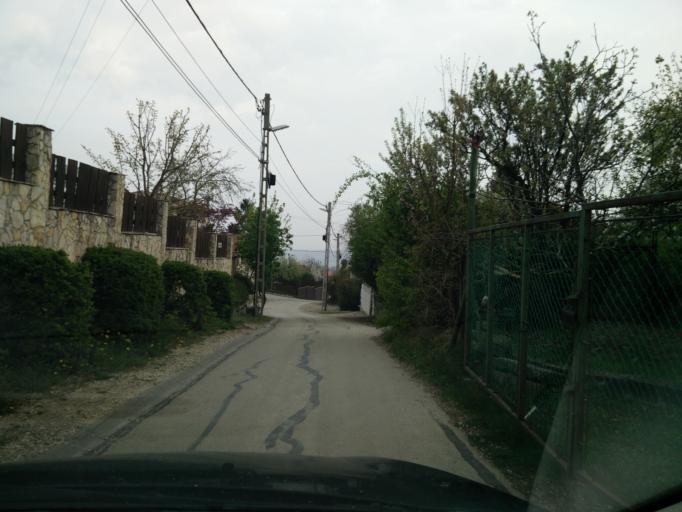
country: HU
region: Pest
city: Budaors
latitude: 47.4684
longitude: 18.9576
